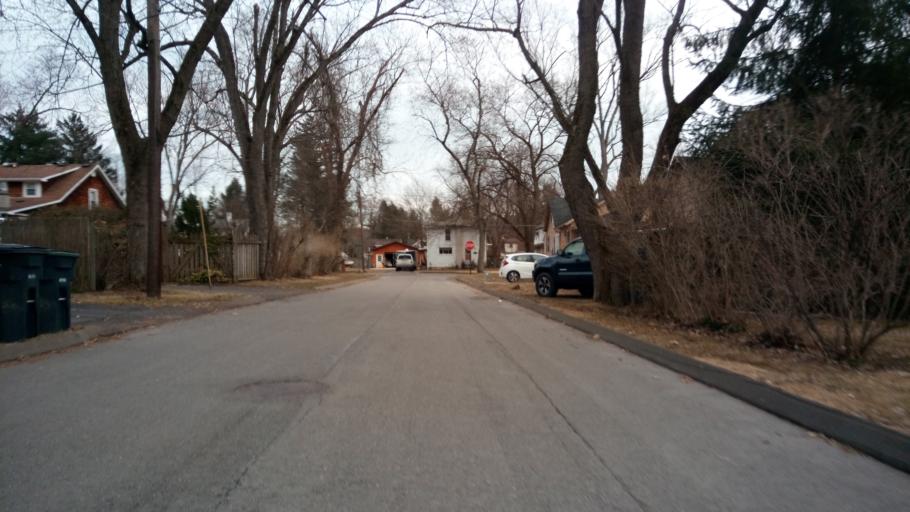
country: US
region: New York
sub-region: Chemung County
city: West Elmira
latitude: 42.0800
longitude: -76.8595
